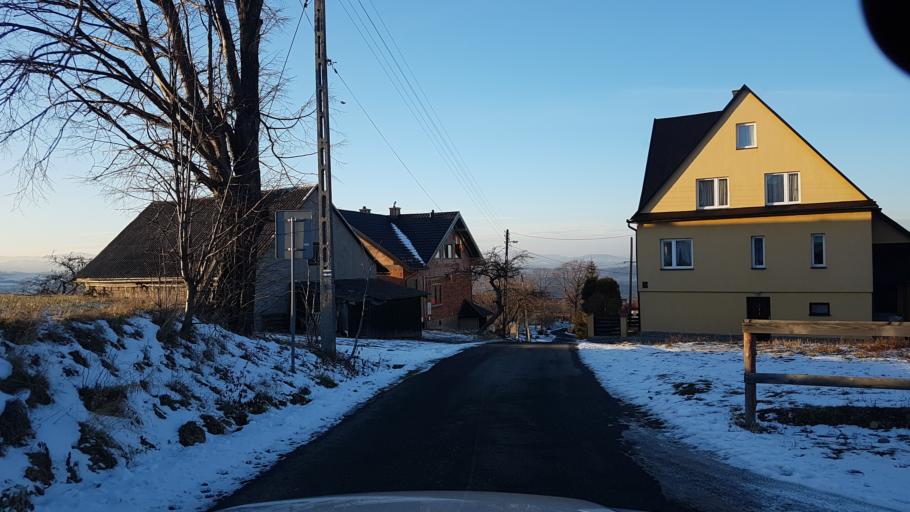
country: PL
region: Lesser Poland Voivodeship
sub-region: Powiat nowosadecki
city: Rytro
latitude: 49.5108
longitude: 20.6721
